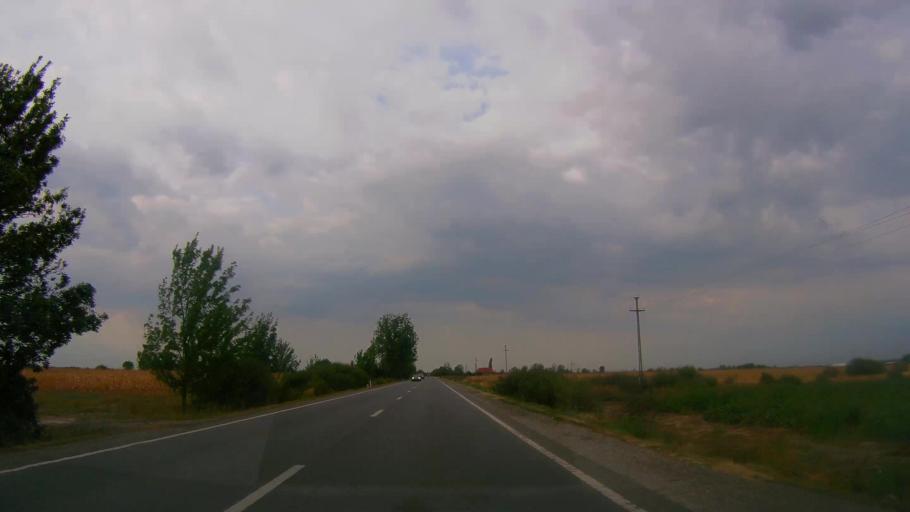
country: RO
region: Satu Mare
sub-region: Comuna Botiz
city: Botiz
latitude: 47.8505
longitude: 22.9725
